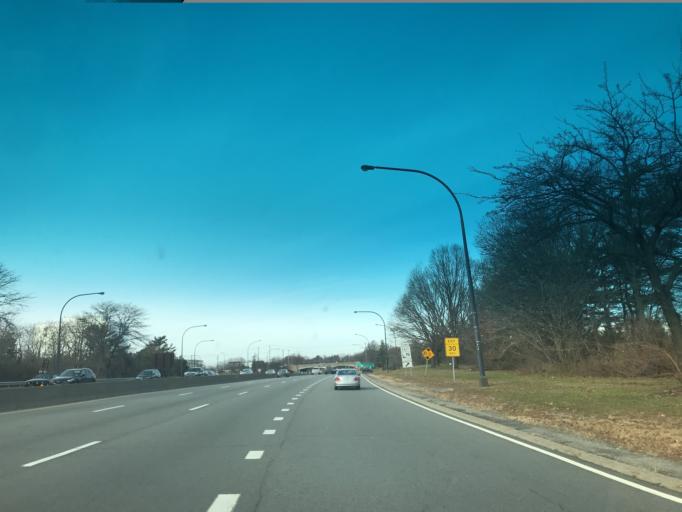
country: US
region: New York
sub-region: Nassau County
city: Carle Place
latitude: 40.7404
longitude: -73.6104
